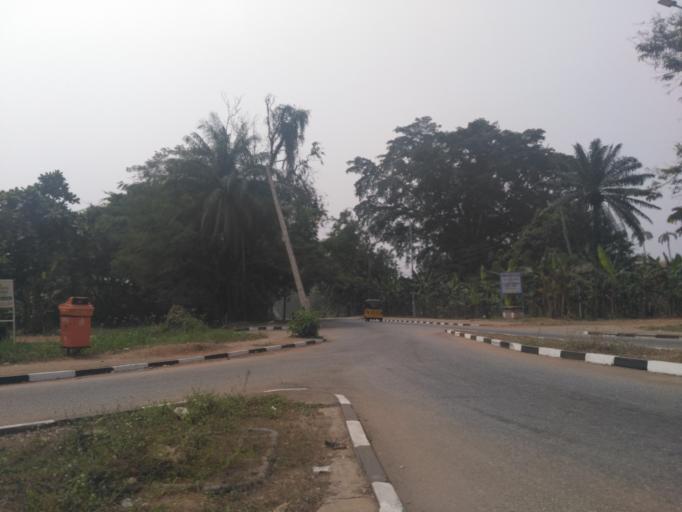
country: GH
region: Ashanti
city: Kumasi
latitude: 6.6823
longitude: -1.6260
